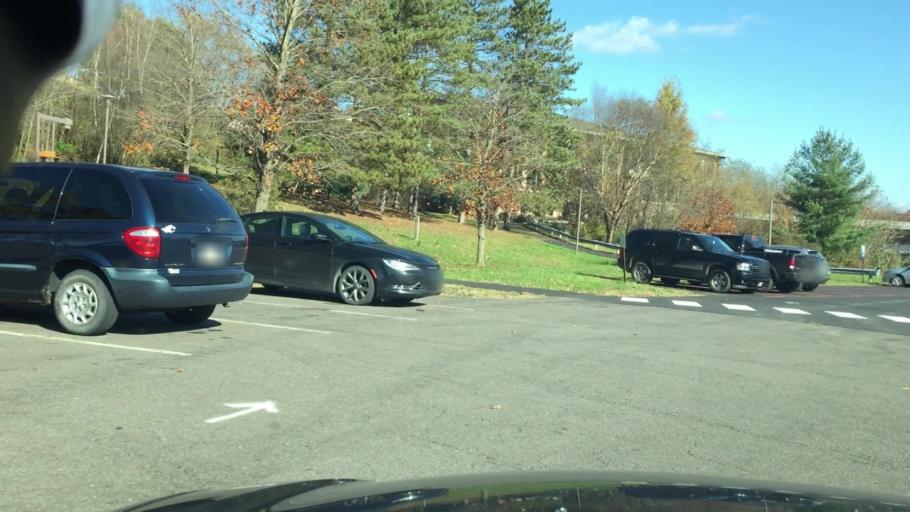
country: US
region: Pennsylvania
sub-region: Luzerne County
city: Nanticoke
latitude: 41.1921
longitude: -75.9946
